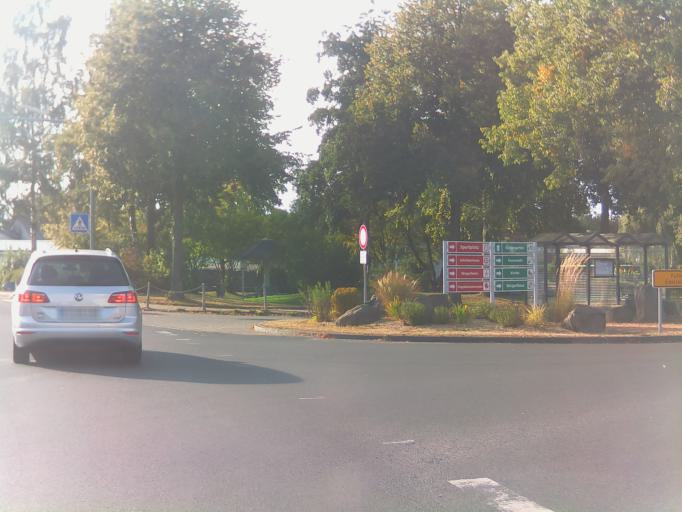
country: DE
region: Hesse
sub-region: Regierungsbezirk Kassel
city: Eichenzell
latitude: 50.5162
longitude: 9.7125
